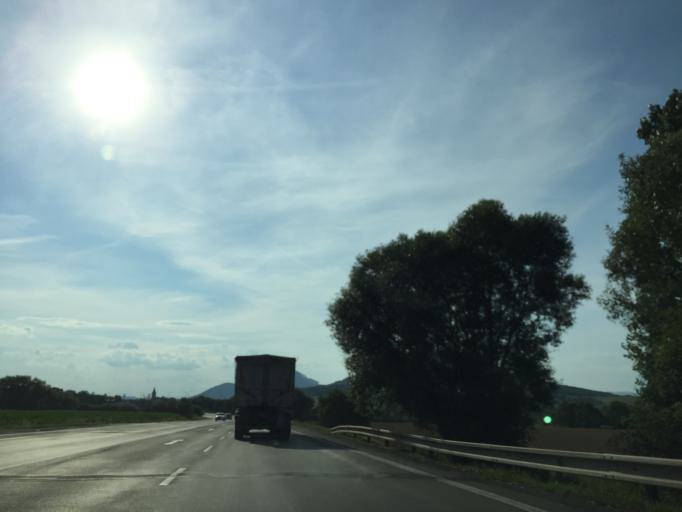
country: SK
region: Presovsky
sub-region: Okres Presov
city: Presov
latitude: 49.0446
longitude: 21.3465
